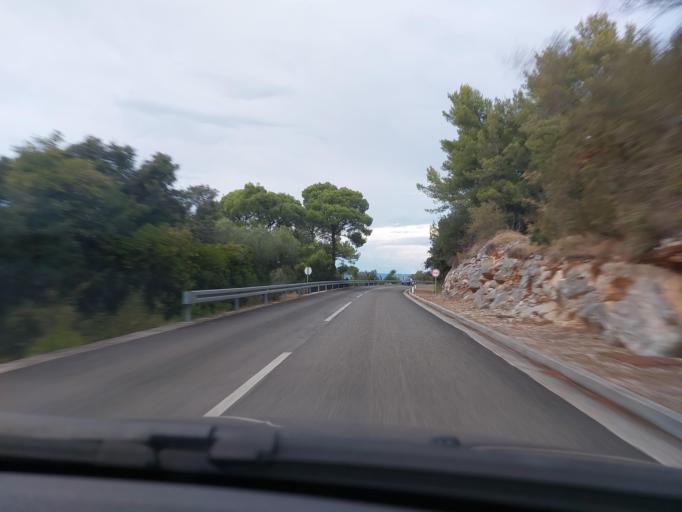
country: HR
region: Dubrovacko-Neretvanska
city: Smokvica
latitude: 42.7682
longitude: 16.8754
